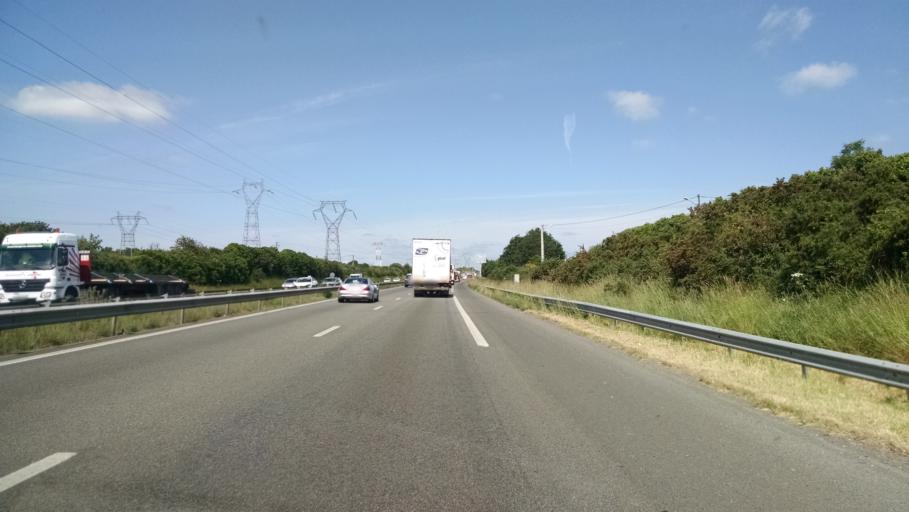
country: FR
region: Pays de la Loire
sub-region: Departement de la Loire-Atlantique
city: Reze
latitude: 47.1632
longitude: -1.5637
